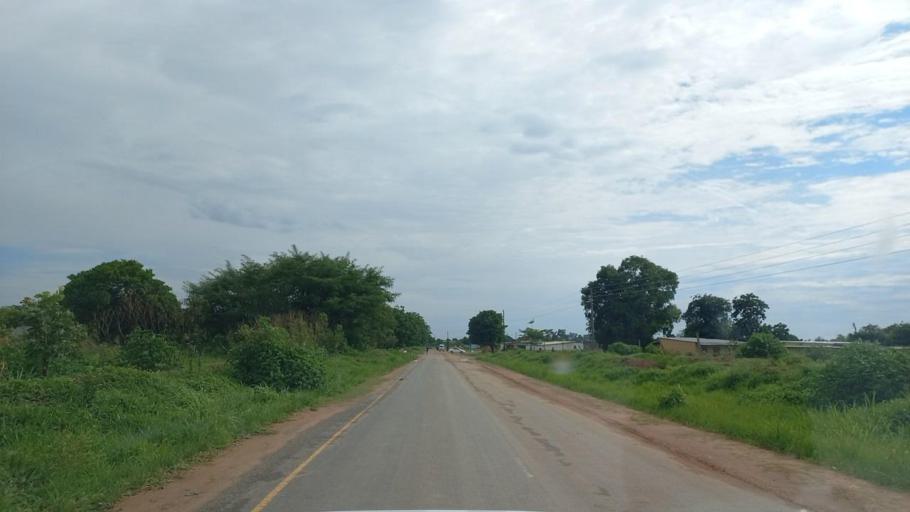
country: ZM
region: Copperbelt
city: Kitwe
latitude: -12.8803
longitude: 28.3223
